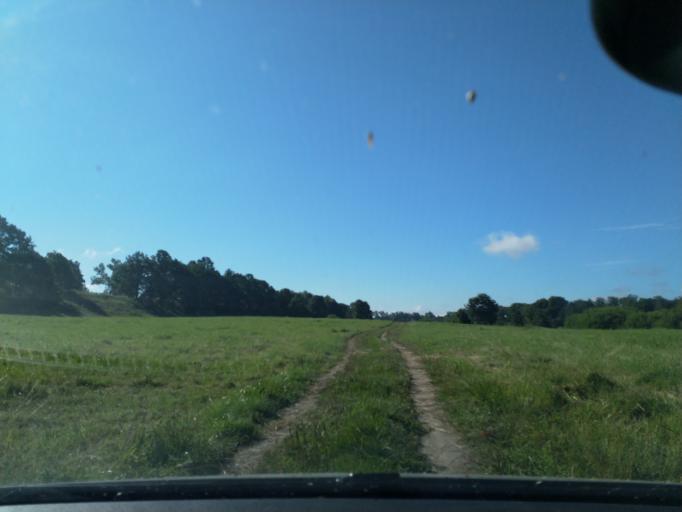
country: LV
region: Kuldigas Rajons
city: Kuldiga
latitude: 56.9756
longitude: 21.9739
